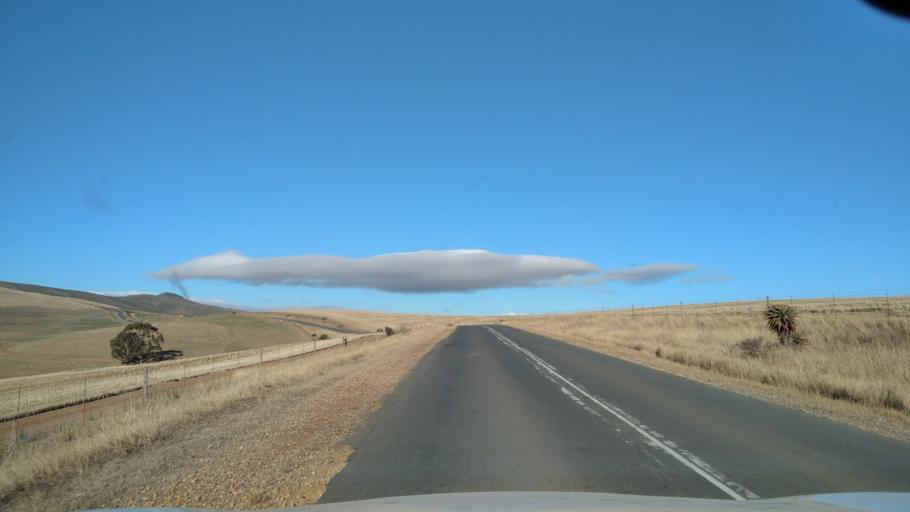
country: ZA
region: Western Cape
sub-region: Overberg District Municipality
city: Caledon
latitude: -34.1662
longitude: 19.2955
